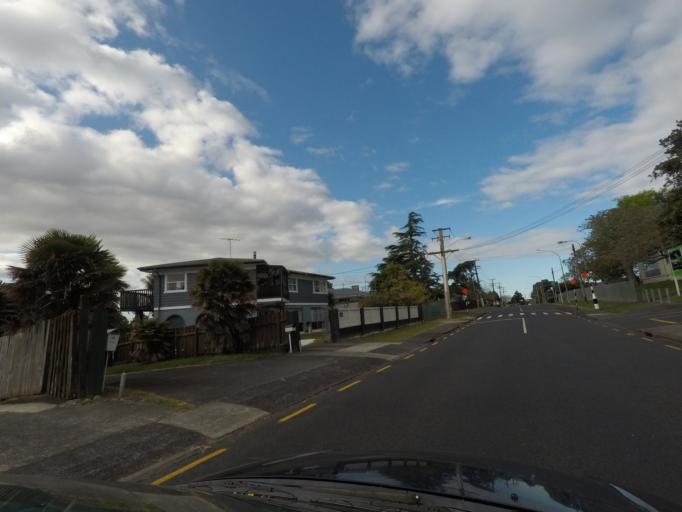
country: NZ
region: Auckland
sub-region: Auckland
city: Rosebank
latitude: -36.8870
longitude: 174.6544
